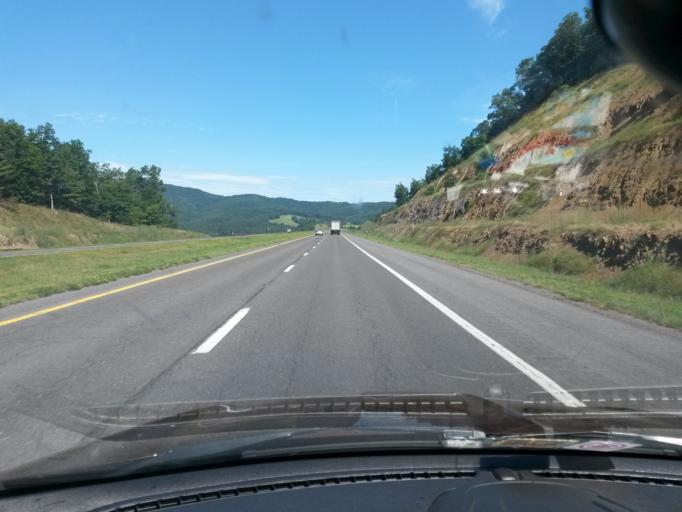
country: US
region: West Virginia
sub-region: Hardy County
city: Moorefield
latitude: 39.0644
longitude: -78.7924
